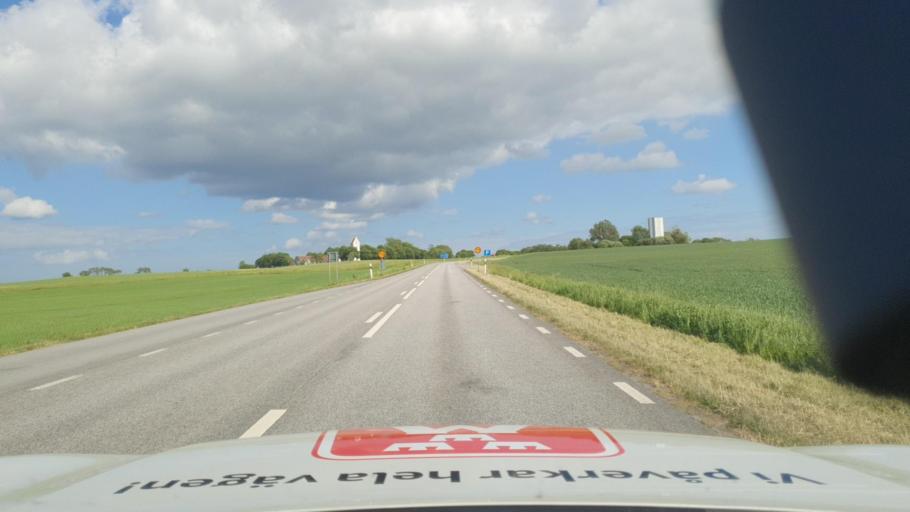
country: SE
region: Skane
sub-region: Simrishamns Kommun
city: Kivik
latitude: 55.5568
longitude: 14.1615
